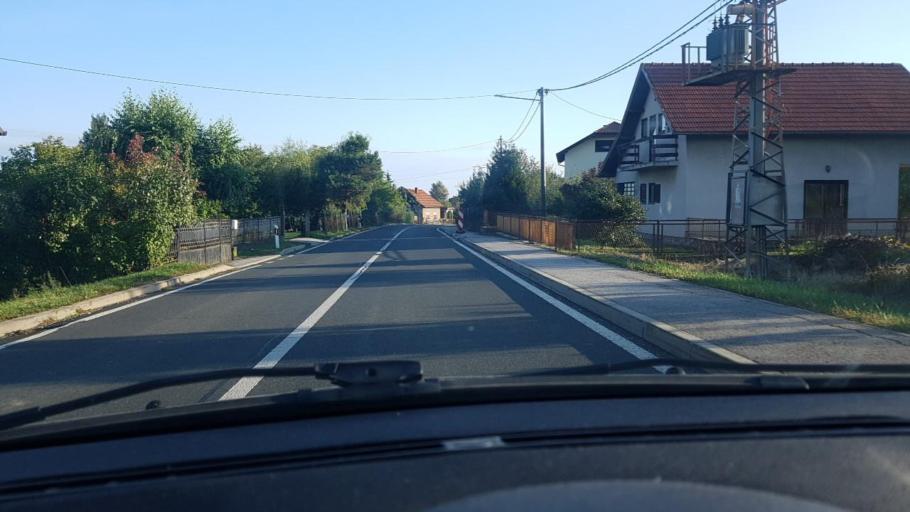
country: HR
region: Krapinsko-Zagorska
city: Marija Bistrica
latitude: 45.9643
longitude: 16.0925
